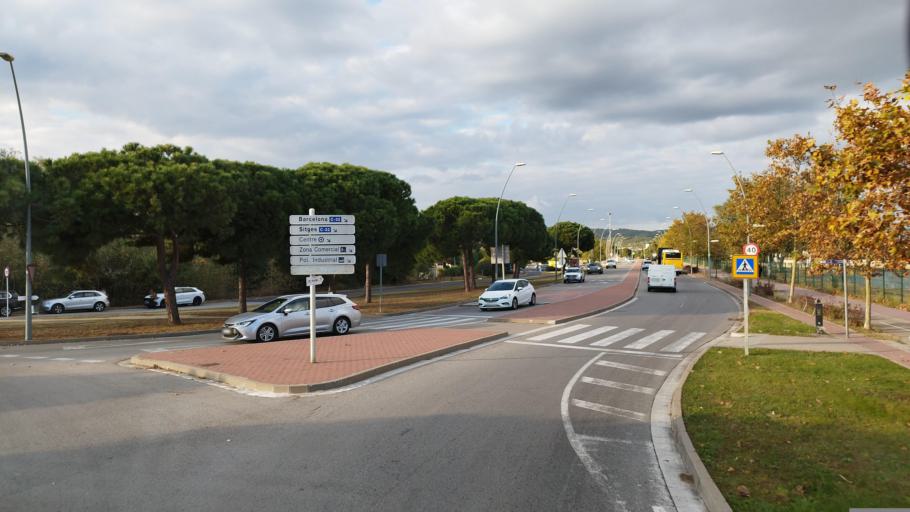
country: ES
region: Catalonia
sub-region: Provincia de Barcelona
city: Castelldefels
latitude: 41.2740
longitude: 1.9911
